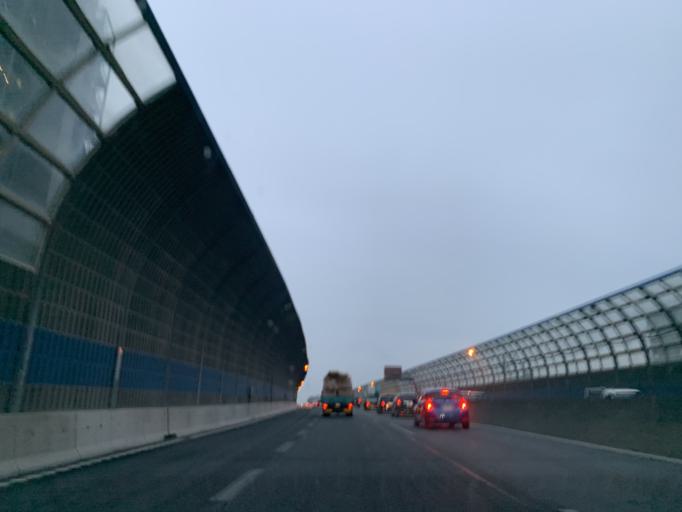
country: JP
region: Chiba
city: Funabashi
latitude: 35.6885
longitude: 139.9969
